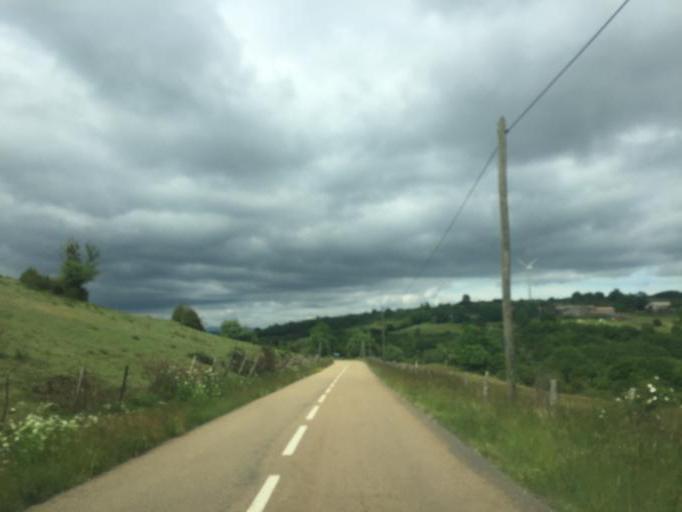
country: FR
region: Rhone-Alpes
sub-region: Departement de l'Ardeche
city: Saint-Priest
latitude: 44.6852
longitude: 4.5492
